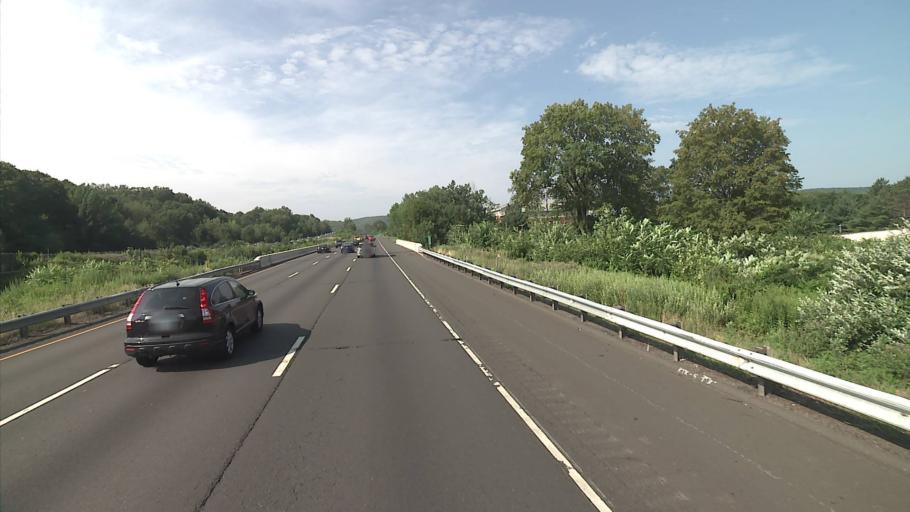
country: US
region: Connecticut
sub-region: Middlesex County
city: Middletown
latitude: 41.5843
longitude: -72.7137
